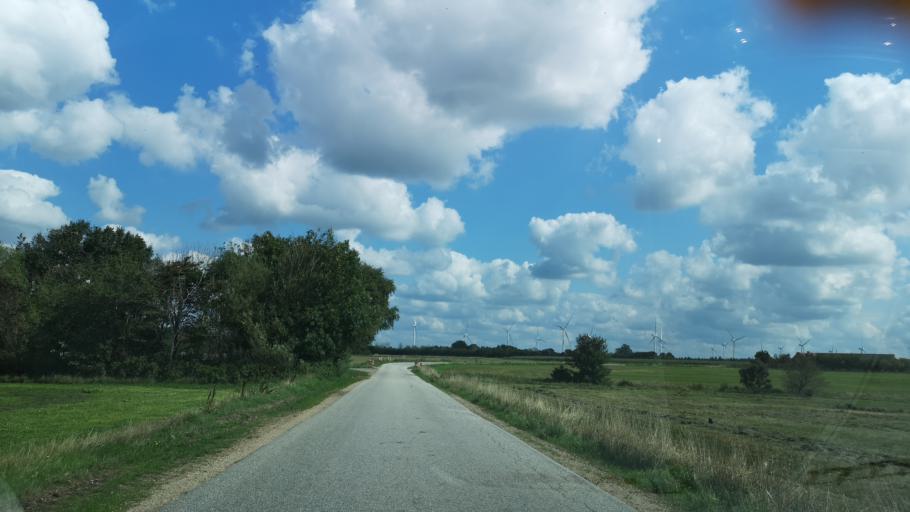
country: DK
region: Central Jutland
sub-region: Ringkobing-Skjern Kommune
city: Skjern
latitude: 55.8510
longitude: 8.3780
